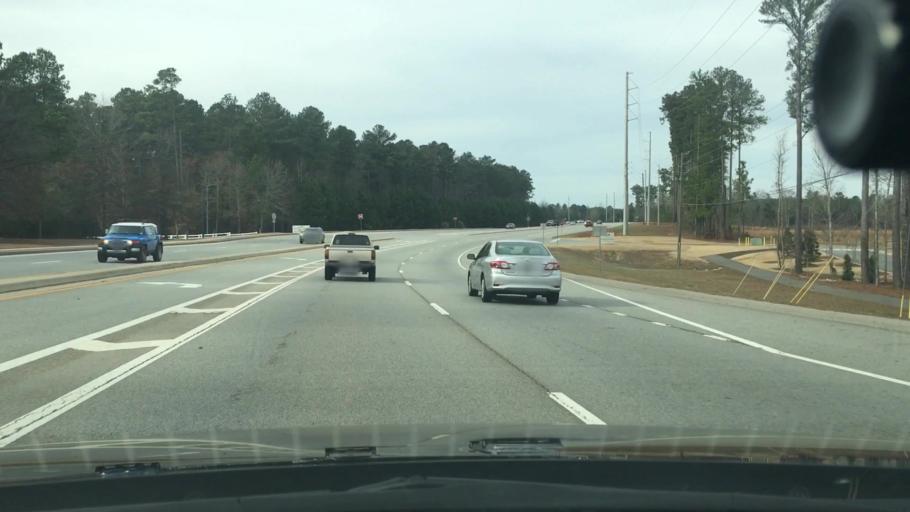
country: US
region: Georgia
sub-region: Coweta County
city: Senoia
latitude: 33.3446
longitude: -84.5456
